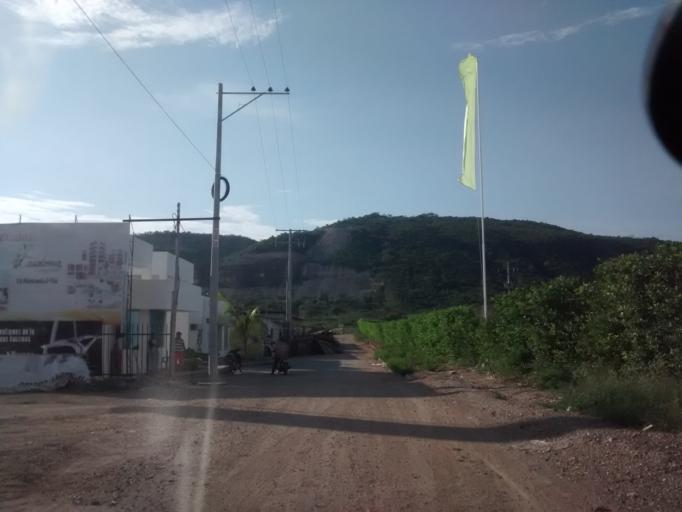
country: CO
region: Cundinamarca
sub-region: Girardot
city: Girardot City
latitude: 4.3031
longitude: -74.8205
